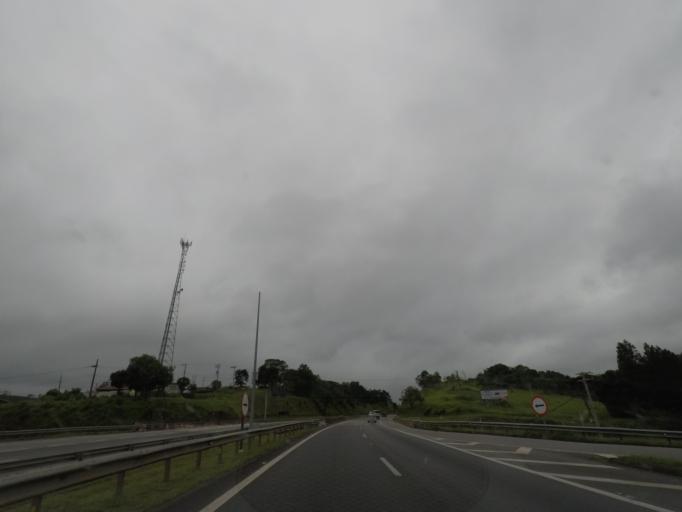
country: BR
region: Sao Paulo
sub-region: Bom Jesus Dos Perdoes
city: Bom Jesus dos Perdoes
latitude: -23.1682
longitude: -46.3947
